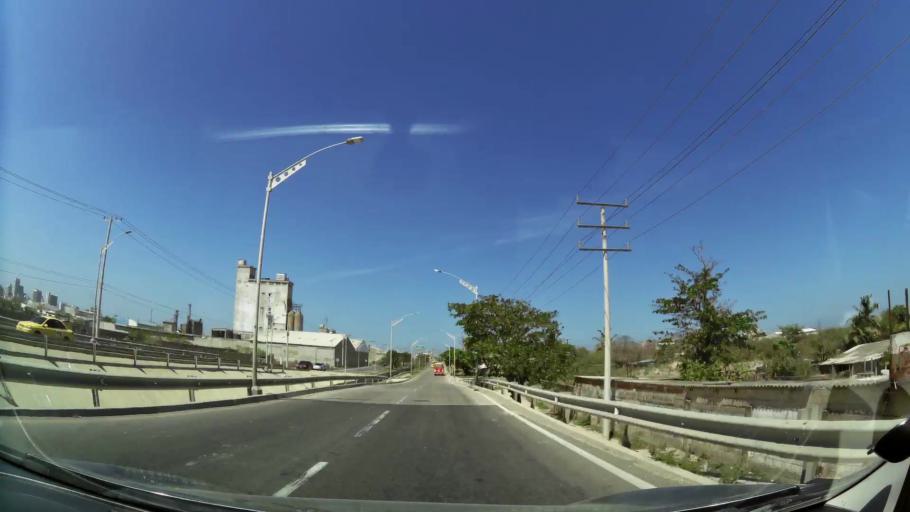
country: CO
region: Atlantico
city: Barranquilla
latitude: 10.9781
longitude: -74.7693
